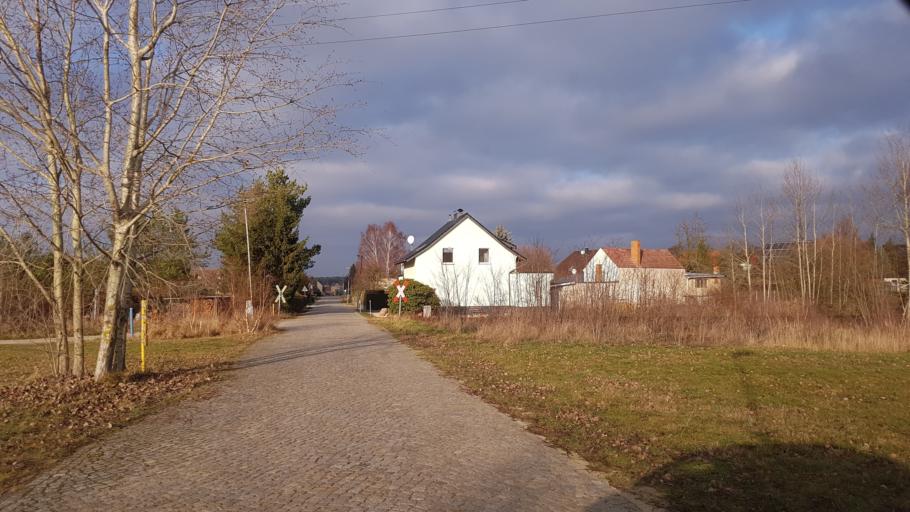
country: DE
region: Brandenburg
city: Sallgast
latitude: 51.5925
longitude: 13.7863
